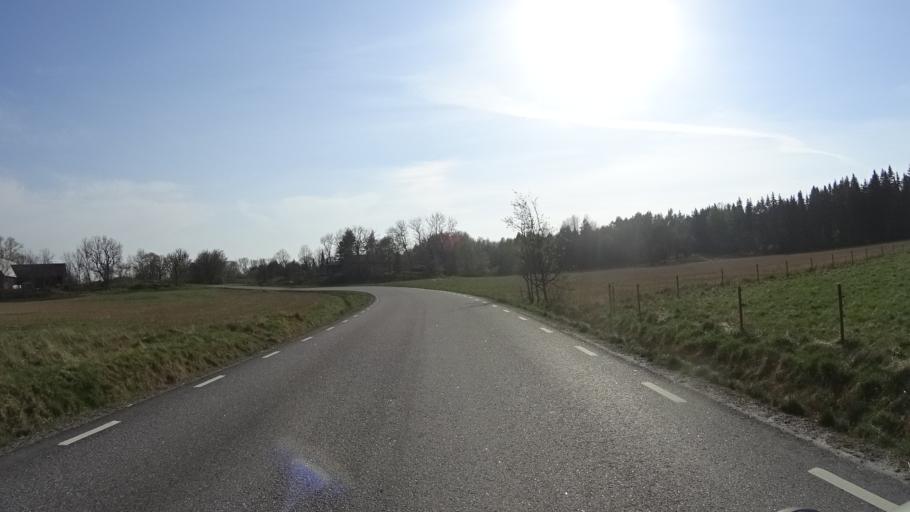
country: SE
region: Vaestra Goetaland
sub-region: Gotene Kommun
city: Goetene
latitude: 58.6233
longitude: 13.4966
